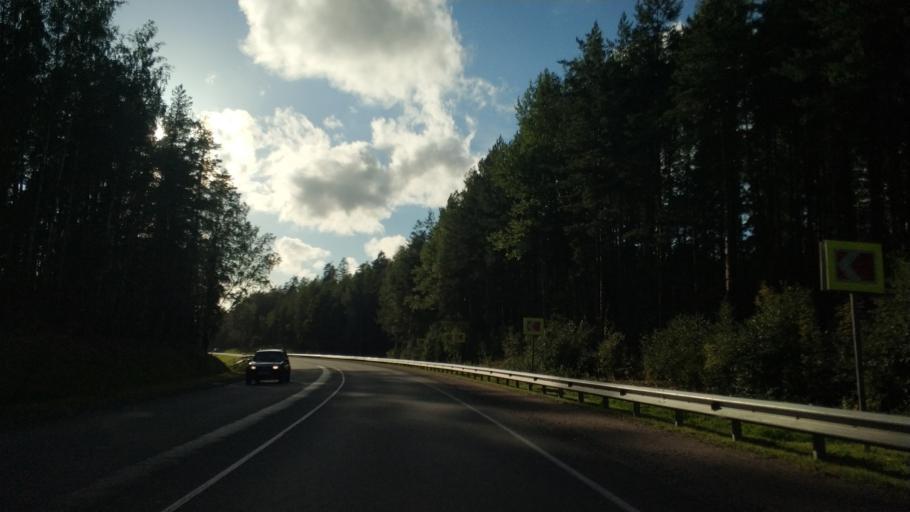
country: RU
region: Leningrad
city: Sapernoye
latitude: 60.7157
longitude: 30.0094
